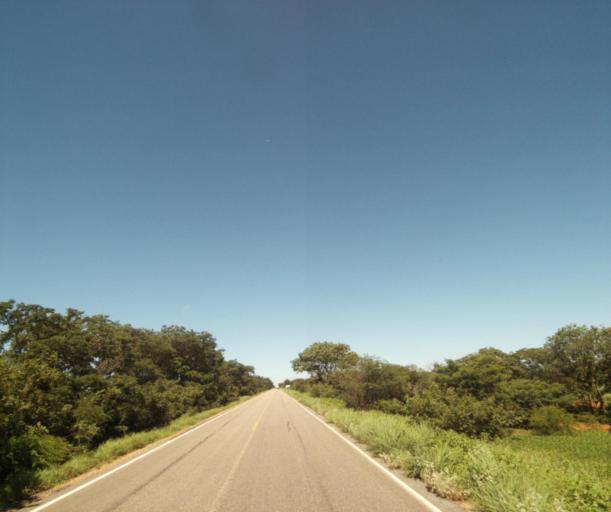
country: BR
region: Bahia
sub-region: Palmas De Monte Alto
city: Palmas de Monte Alto
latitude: -14.2640
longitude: -43.3399
